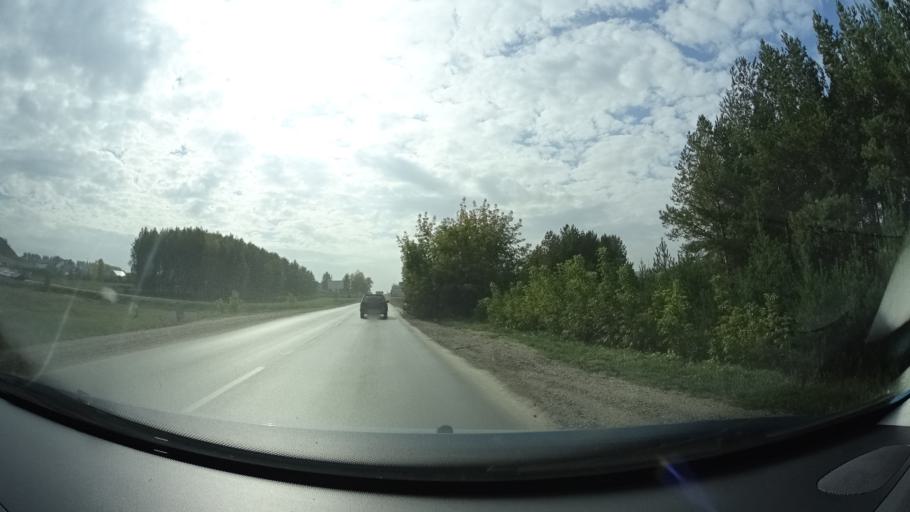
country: RU
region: Bashkortostan
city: Oktyabr'skiy
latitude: 54.5220
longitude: 53.5419
